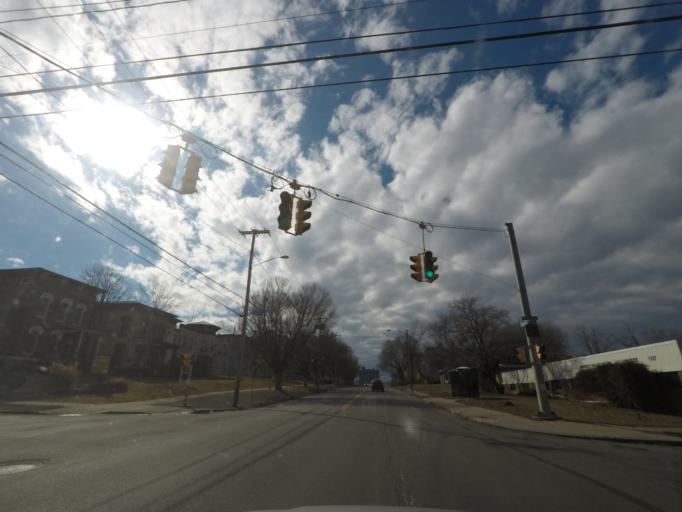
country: US
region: New York
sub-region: Onondaga County
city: Syracuse
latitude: 43.0469
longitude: -76.1320
